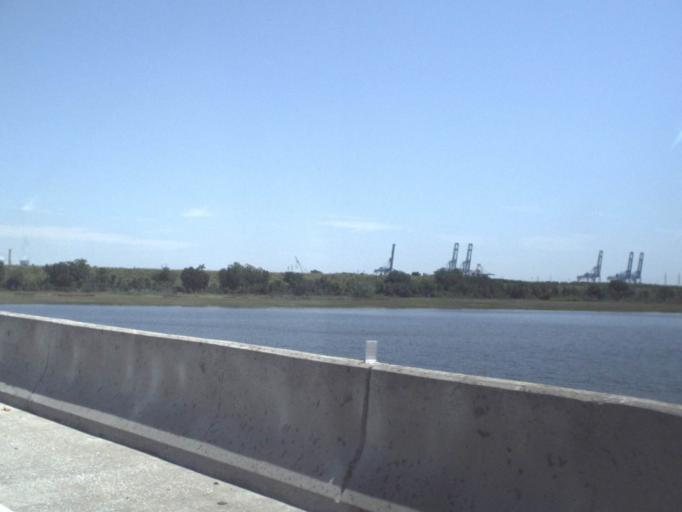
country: US
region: Florida
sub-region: Duval County
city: Jacksonville
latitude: 30.3742
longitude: -81.5524
